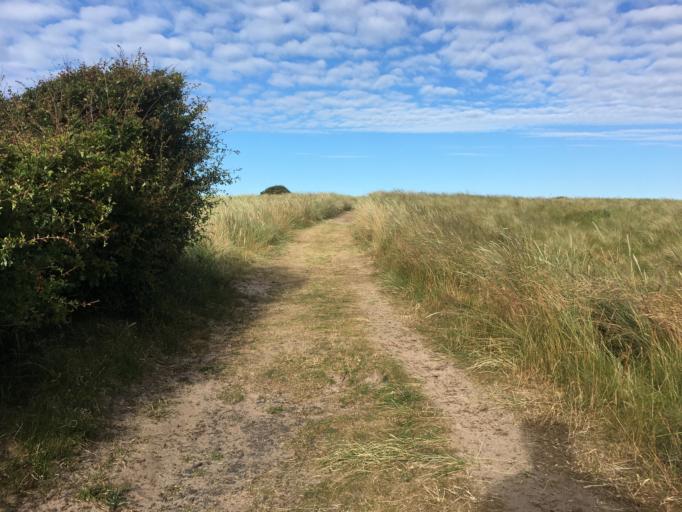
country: GB
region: England
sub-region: Northumberland
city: Bamburgh
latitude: 55.6169
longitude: -1.7422
